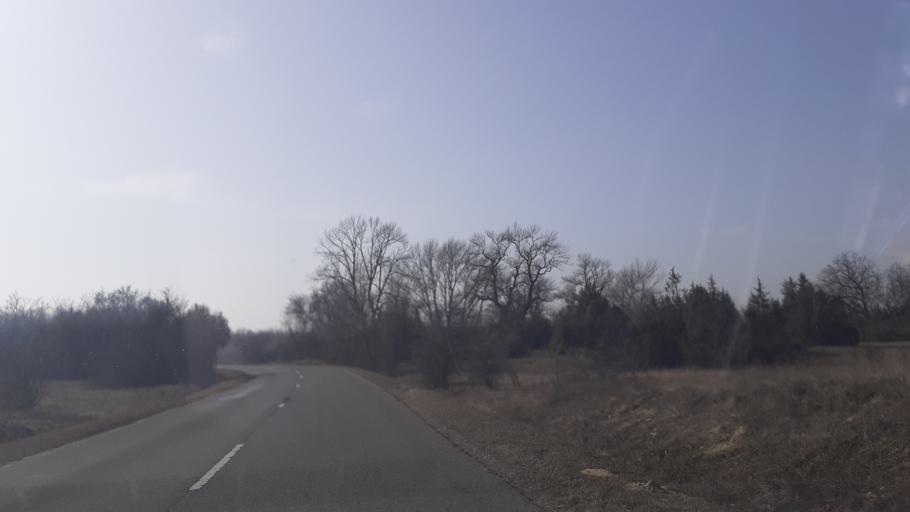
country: HU
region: Pest
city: Orkeny
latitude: 47.0985
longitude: 19.3880
